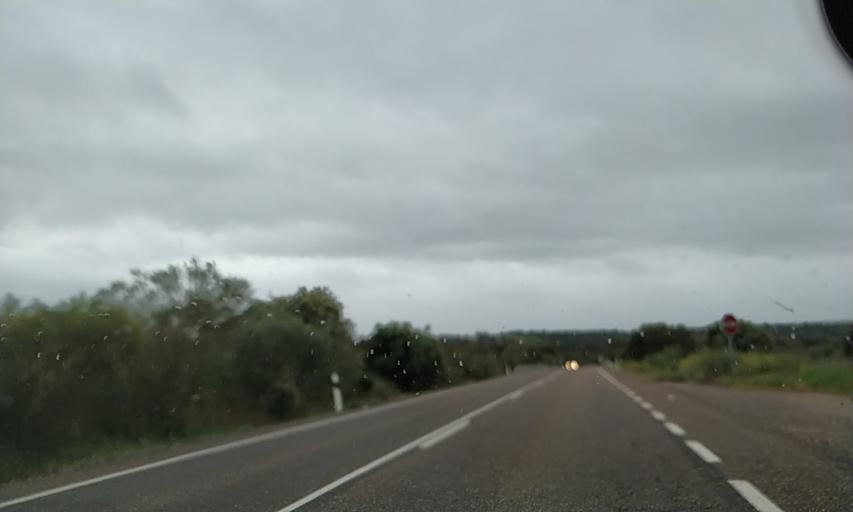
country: ES
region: Extremadura
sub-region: Provincia de Badajoz
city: La Roca de la Sierra
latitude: 39.1293
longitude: -6.6649
